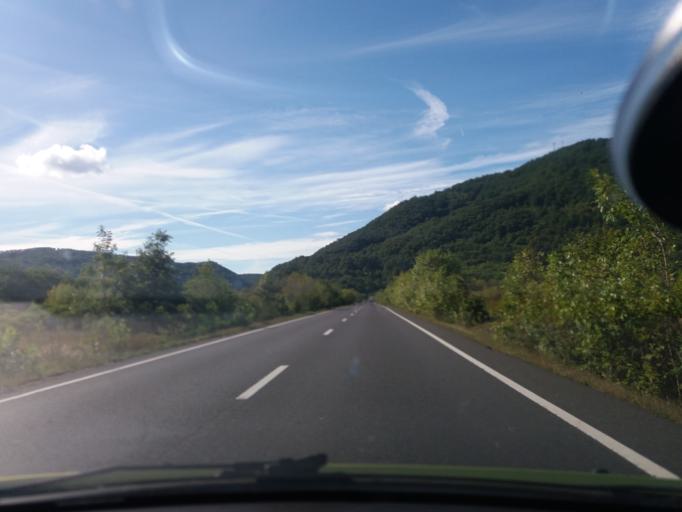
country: RO
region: Hunedoara
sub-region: Comuna Zam
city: Zam
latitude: 45.9718
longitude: 22.4584
